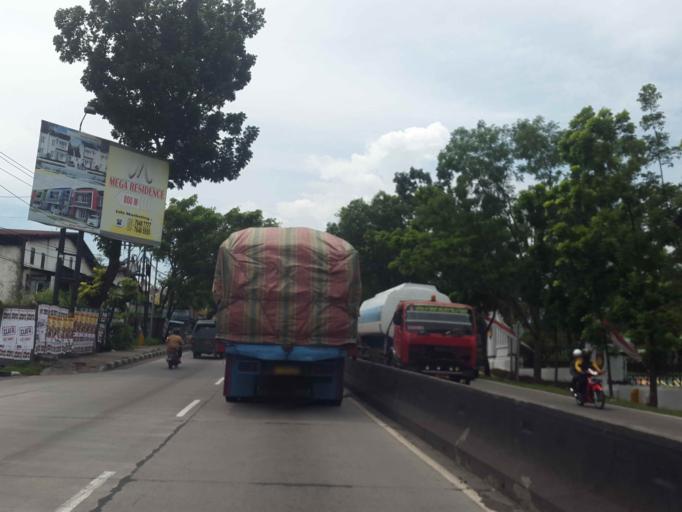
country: ID
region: Central Java
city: Ungaran
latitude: -7.0805
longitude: 110.4111
